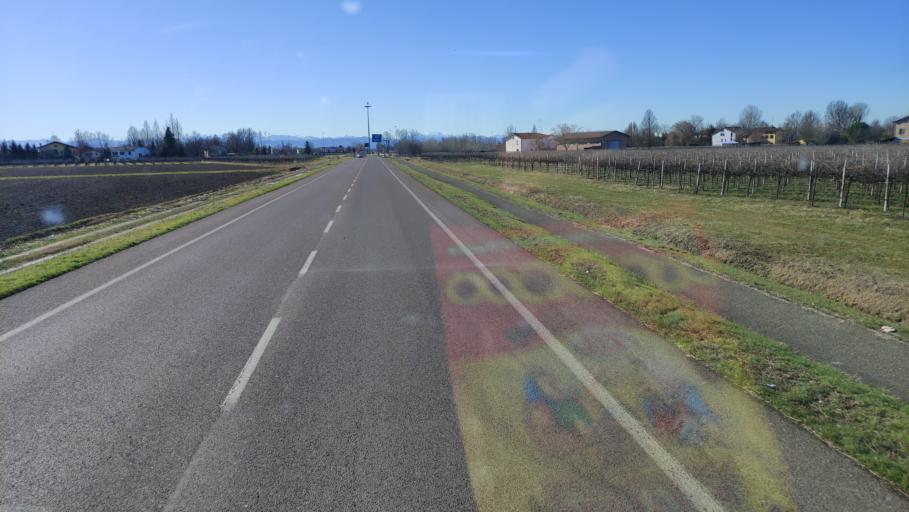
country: IT
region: Emilia-Romagna
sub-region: Provincia di Reggio Emilia
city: San Martino in Rio
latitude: 44.7449
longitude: 10.7780
